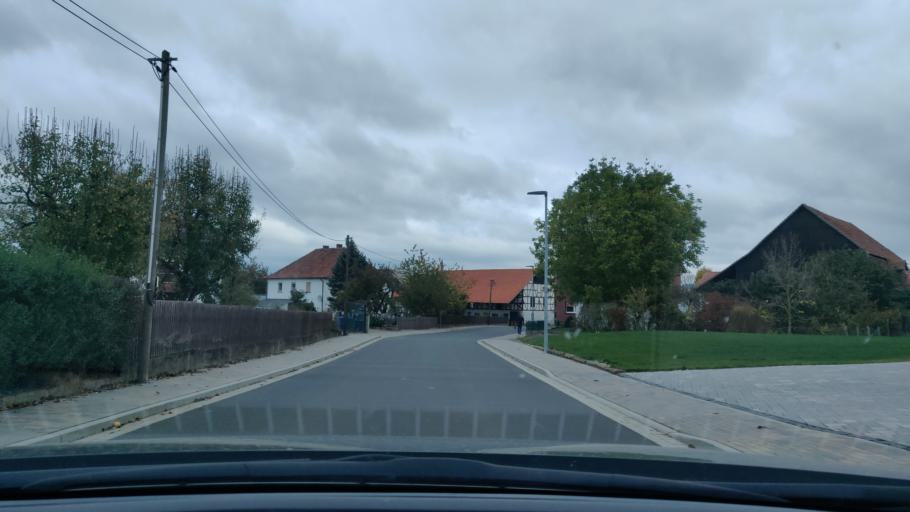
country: DE
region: Hesse
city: Fritzlar
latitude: 51.1805
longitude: 9.2700
